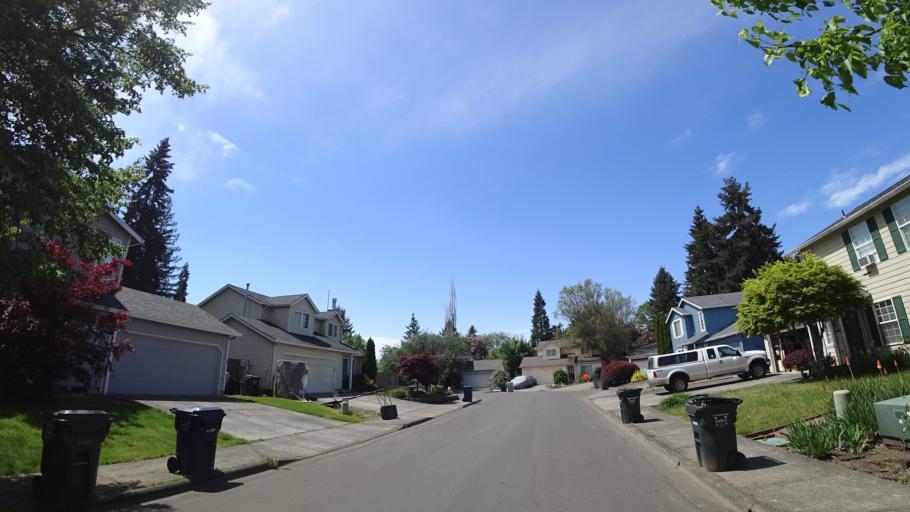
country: US
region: Oregon
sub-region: Washington County
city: Aloha
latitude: 45.4876
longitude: -122.8483
